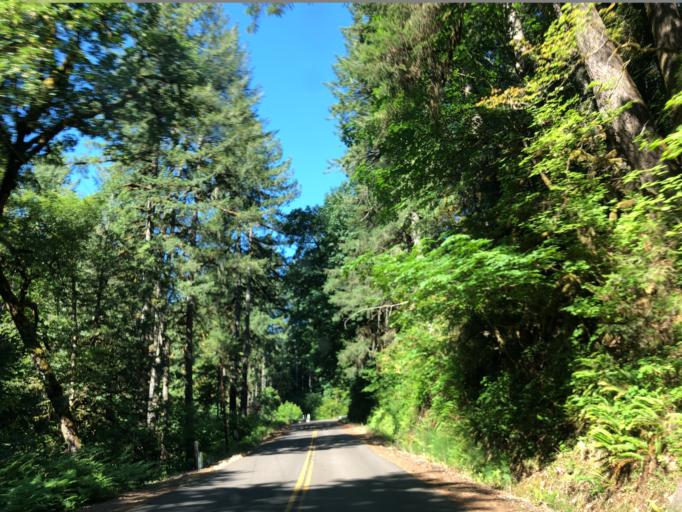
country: US
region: Oregon
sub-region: Linn County
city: Sweet Home
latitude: 44.4660
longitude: -122.6765
